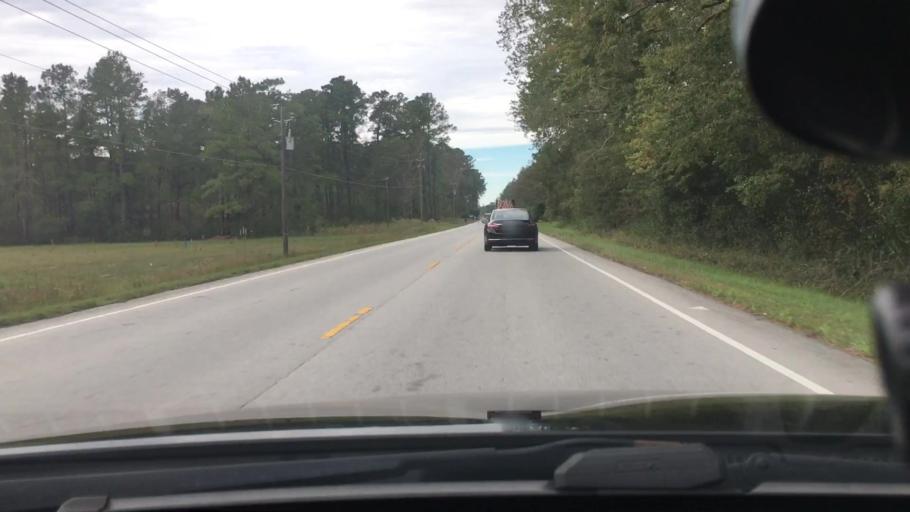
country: US
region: North Carolina
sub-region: Craven County
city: New Bern
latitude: 35.2117
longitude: -77.0618
